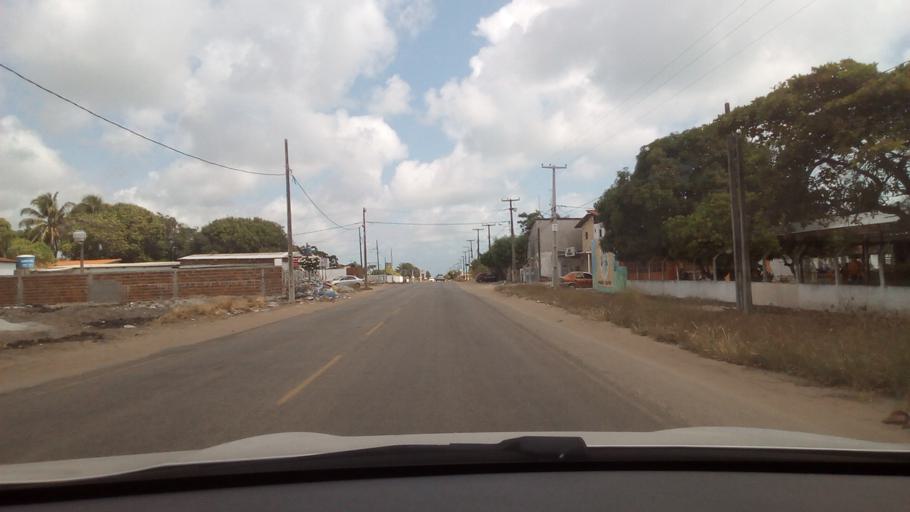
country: BR
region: Paraiba
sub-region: Conde
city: Conde
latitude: -7.2690
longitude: -34.8132
